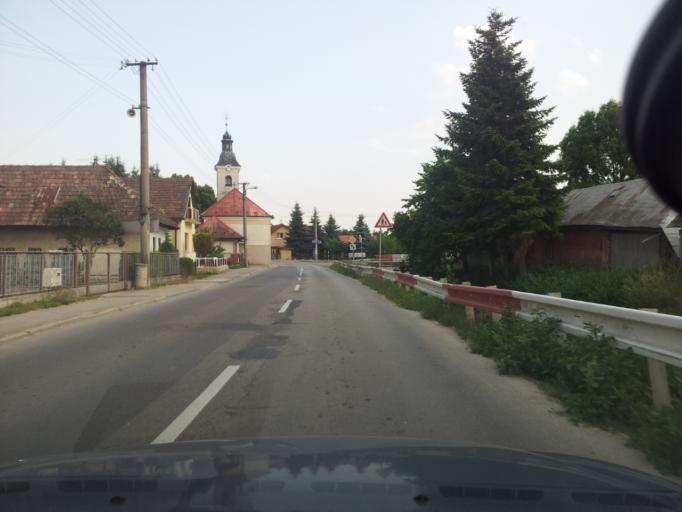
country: SK
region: Nitriansky
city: Banovce nad Bebravou
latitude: 48.7796
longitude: 18.1974
